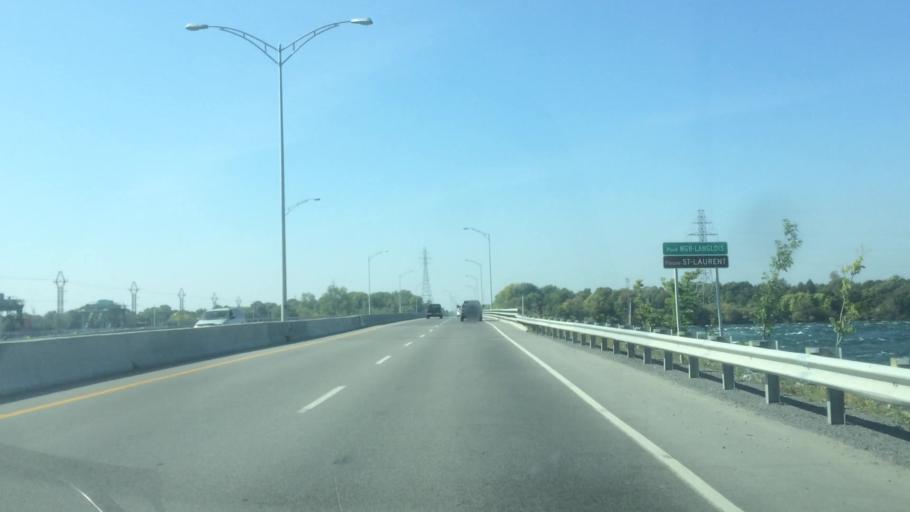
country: CA
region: Quebec
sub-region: Monteregie
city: Salaberry-de-Valleyfield
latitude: 45.2694
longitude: -74.1653
